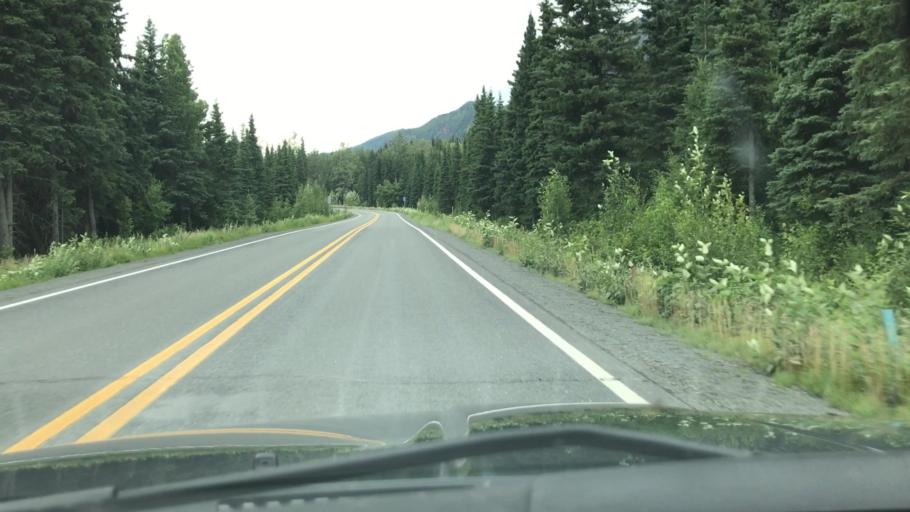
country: US
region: Alaska
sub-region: Kenai Peninsula Borough
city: Seward
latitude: 60.4835
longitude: -149.9428
